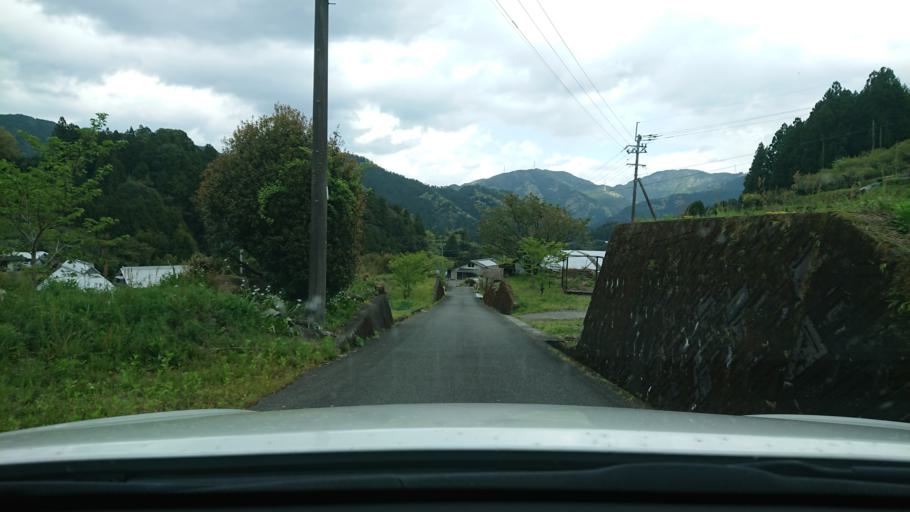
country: JP
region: Tokushima
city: Kamojimacho-jogejima
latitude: 33.8872
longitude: 134.3925
